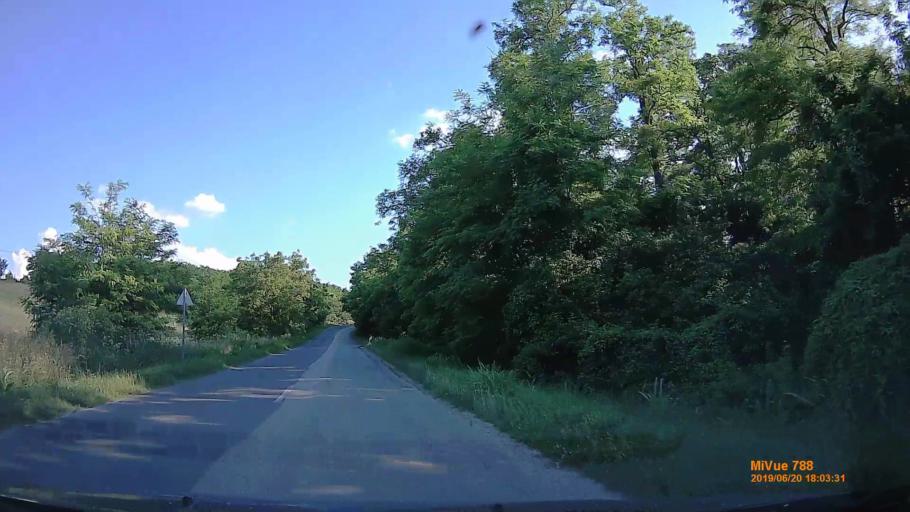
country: HU
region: Baranya
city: Szentlorinc
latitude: 46.0603
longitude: 17.9908
